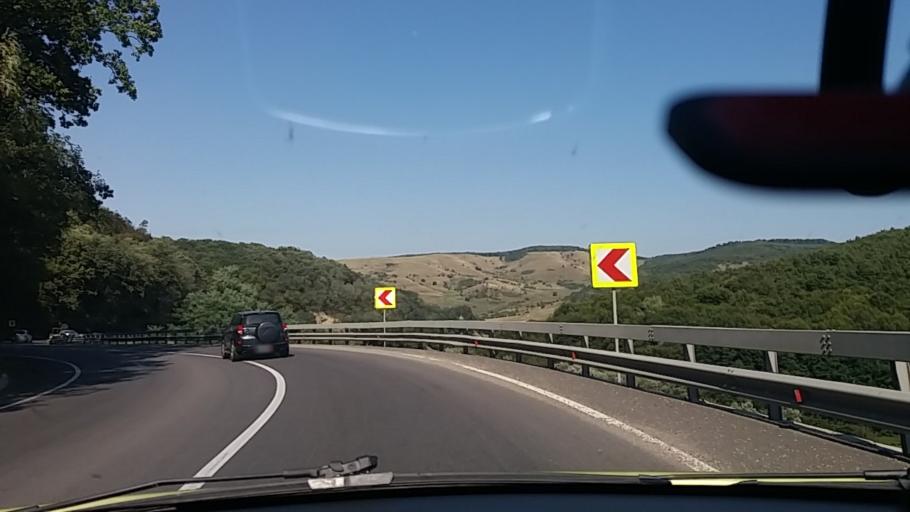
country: RO
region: Sibiu
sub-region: Comuna Slimnic
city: Slimnic
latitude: 45.9419
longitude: 24.1706
